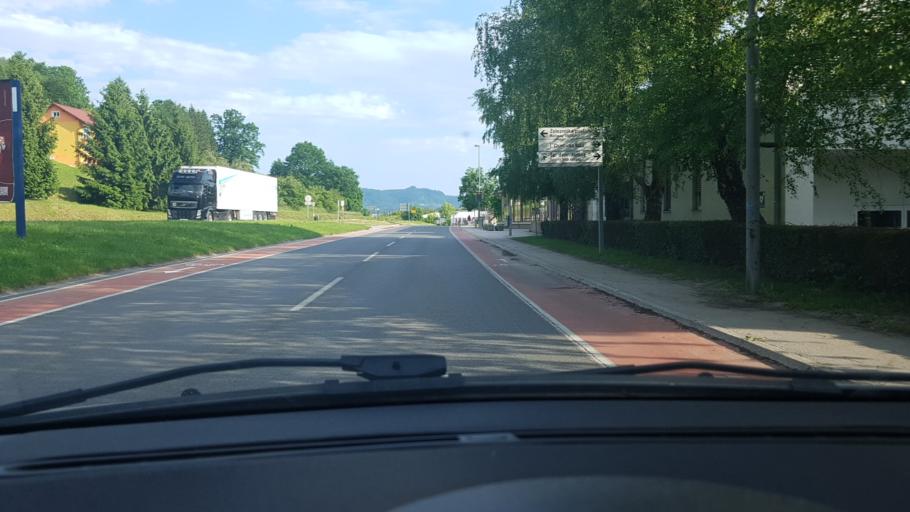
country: SI
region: Rogaska Slatina
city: Rogaska Slatina
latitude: 46.2311
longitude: 15.6381
